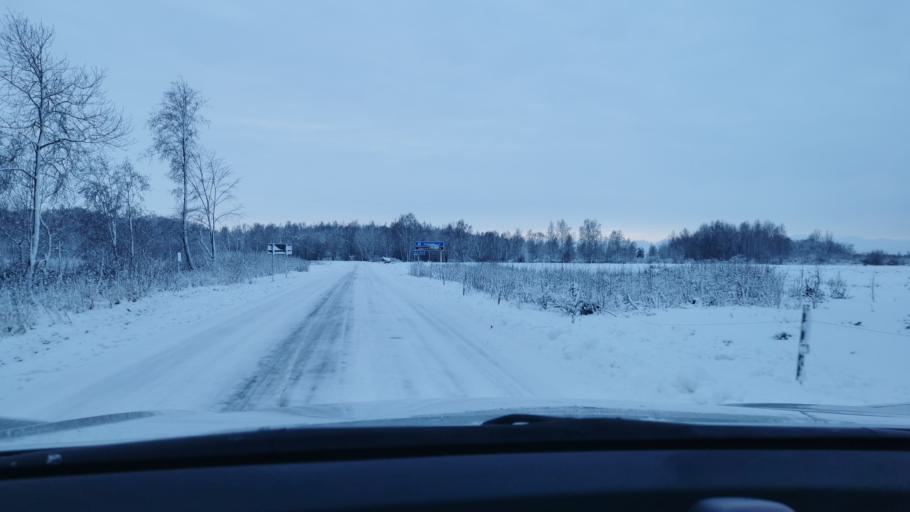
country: EE
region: Laeaene-Virumaa
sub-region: Viru-Nigula vald
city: Kunda
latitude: 59.4475
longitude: 26.5094
